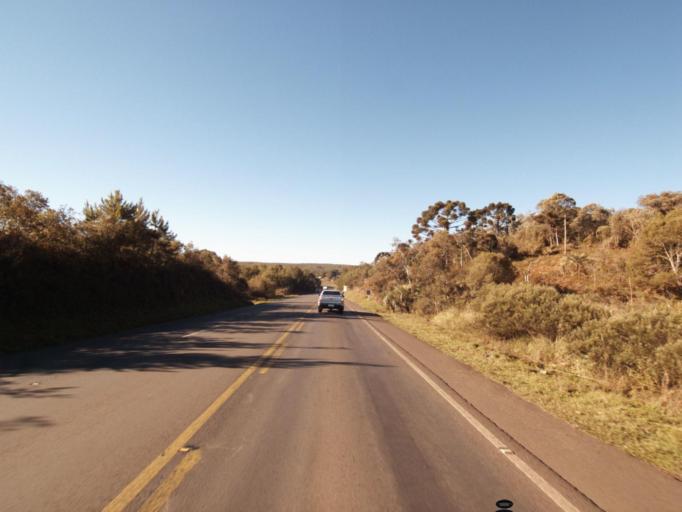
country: BR
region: Santa Catarina
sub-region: Concordia
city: Concordia
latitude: -26.9175
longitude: -51.9567
